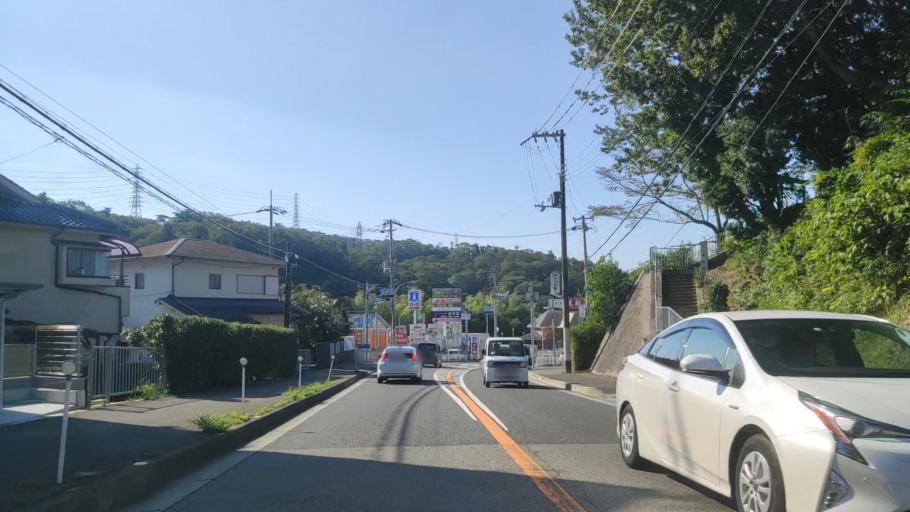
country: JP
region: Hyogo
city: Kobe
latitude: 34.7290
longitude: 135.1602
